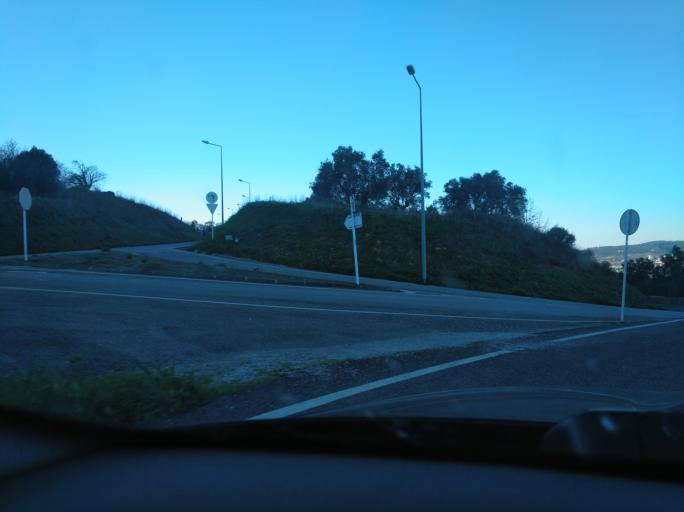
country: PT
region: Lisbon
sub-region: Loures
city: Unhos
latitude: 38.8205
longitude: -9.1171
